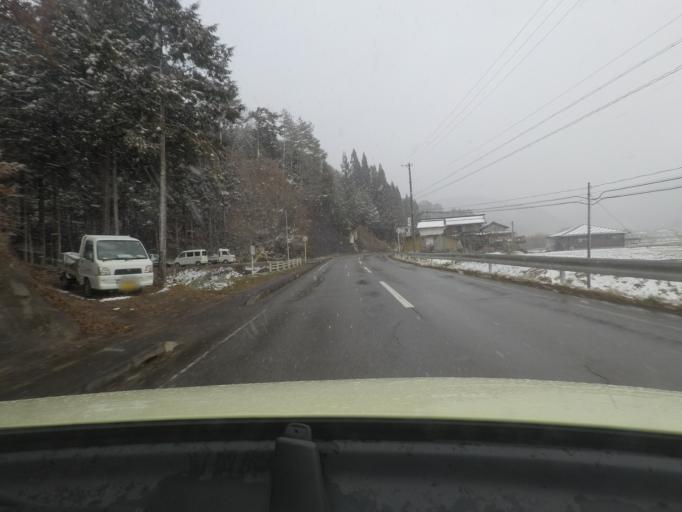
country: JP
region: Gifu
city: Takayama
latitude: 36.1420
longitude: 137.3089
